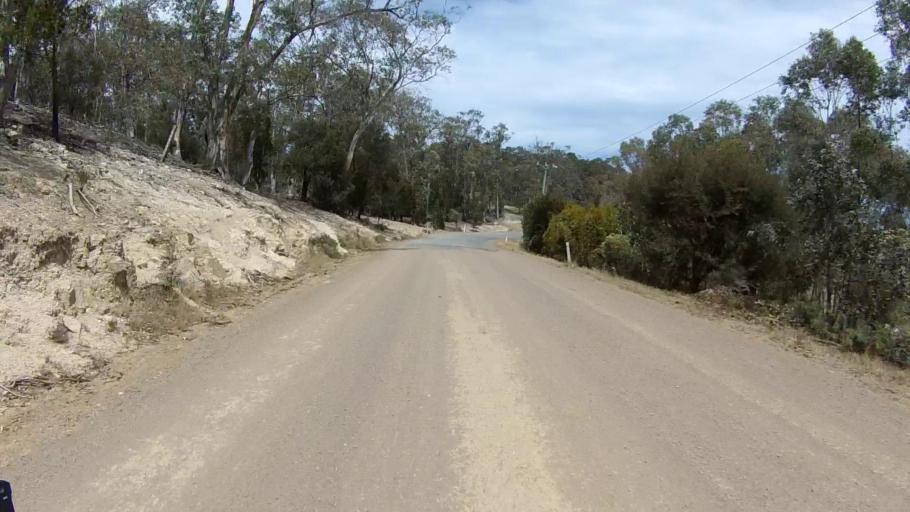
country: AU
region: Tasmania
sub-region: Sorell
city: Sorell
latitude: -42.7997
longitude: 147.6813
